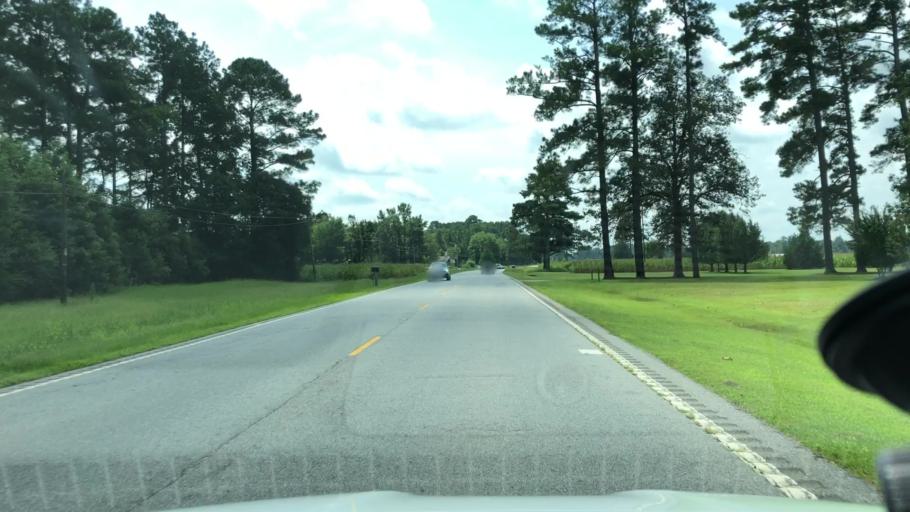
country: US
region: North Carolina
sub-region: Beaufort County
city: Washington
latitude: 35.6666
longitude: -77.0748
